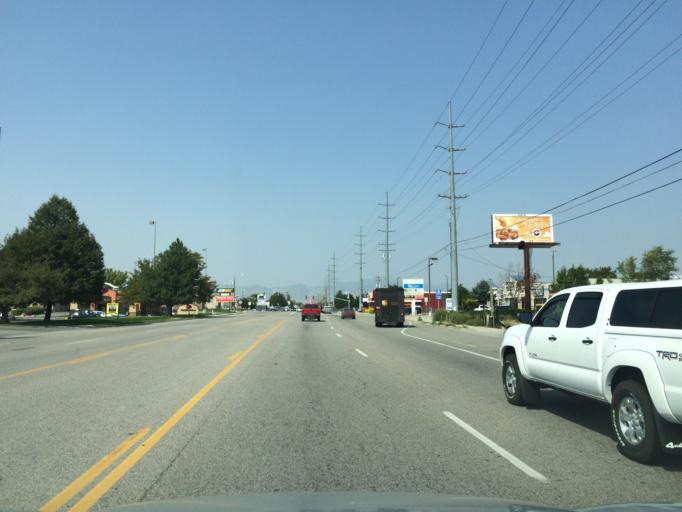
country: US
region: Utah
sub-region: Salt Lake County
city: West Jordan
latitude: 40.5877
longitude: -111.9360
